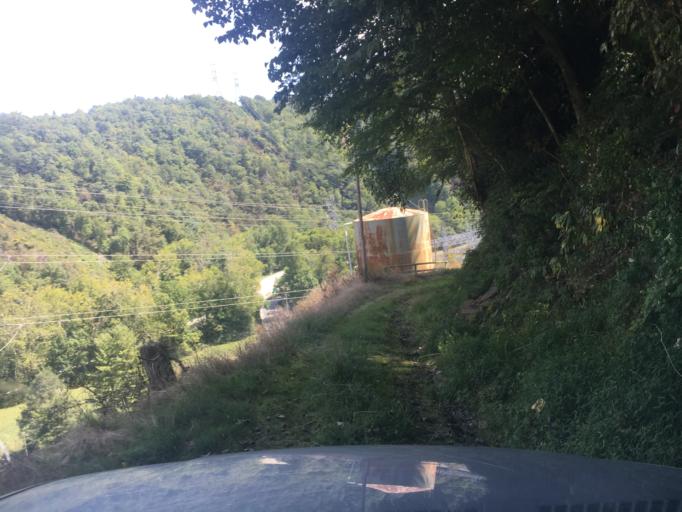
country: US
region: North Carolina
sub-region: Graham County
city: Robbinsville
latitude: 35.2722
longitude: -83.6801
